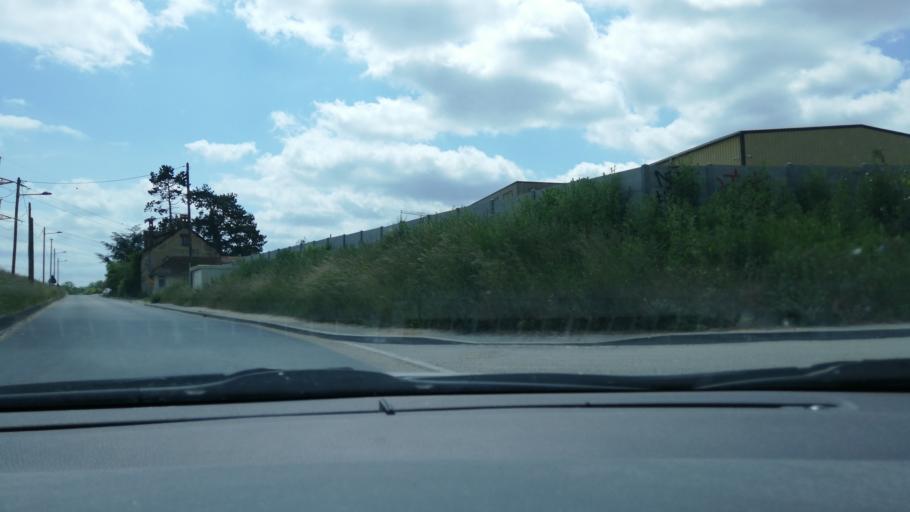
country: FR
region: Ile-de-France
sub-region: Departement du Val-d'Oise
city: Vaureal
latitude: 49.0667
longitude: 2.0223
